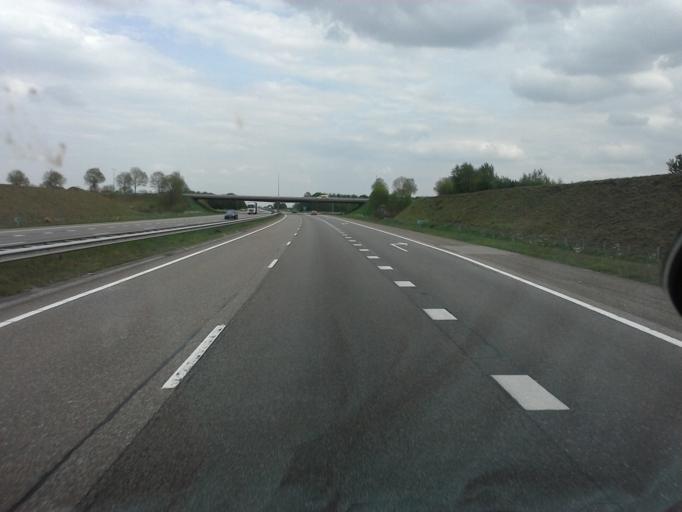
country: NL
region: North Brabant
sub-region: Gemeente Boxmeer
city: Boxmeer
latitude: 51.6618
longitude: 5.9391
